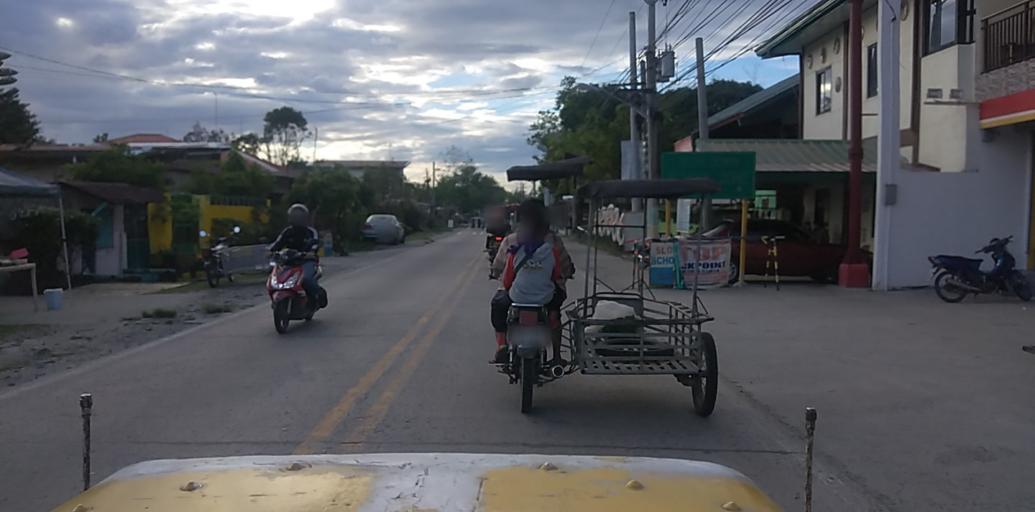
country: PH
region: Central Luzon
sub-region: Province of Pampanga
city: Arayat
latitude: 15.1516
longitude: 120.7428
